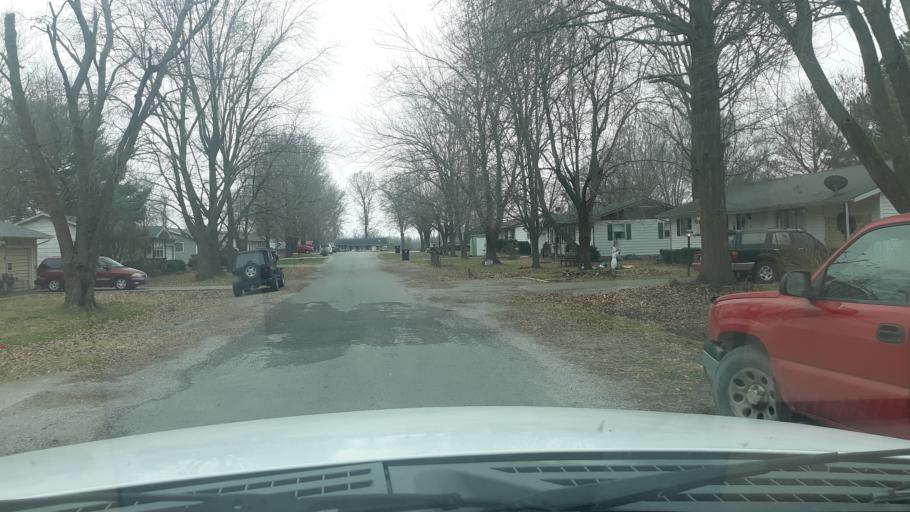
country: US
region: Illinois
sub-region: Saline County
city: Harrisburg
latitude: 37.8362
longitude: -88.6083
